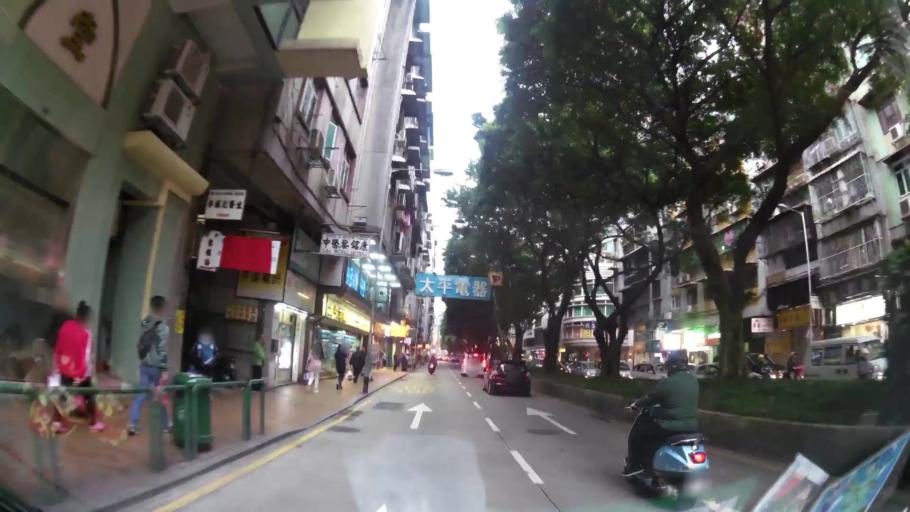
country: MO
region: Macau
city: Macau
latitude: 22.2043
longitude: 113.5455
